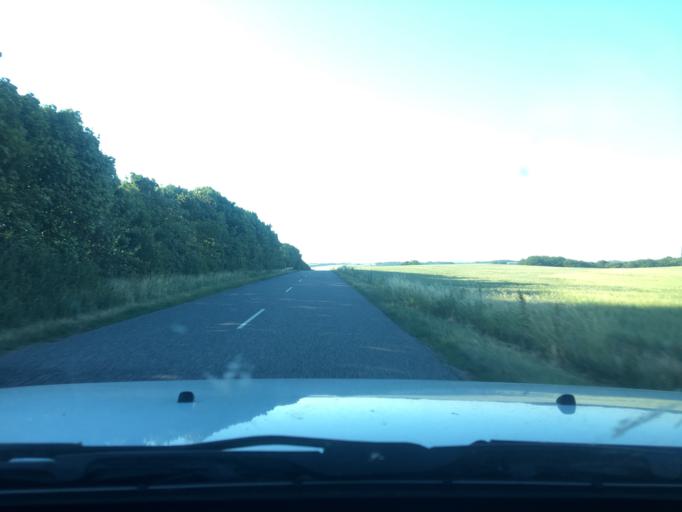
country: DK
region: Central Jutland
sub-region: Favrskov Kommune
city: Hadsten
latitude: 56.3957
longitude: 10.0737
